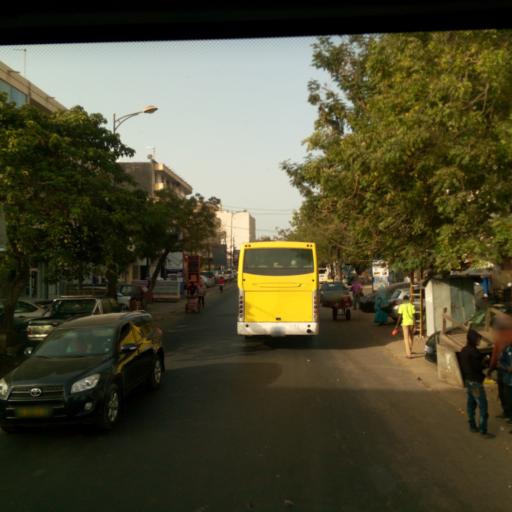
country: SN
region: Dakar
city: Dakar
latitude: 14.6764
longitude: -17.4465
